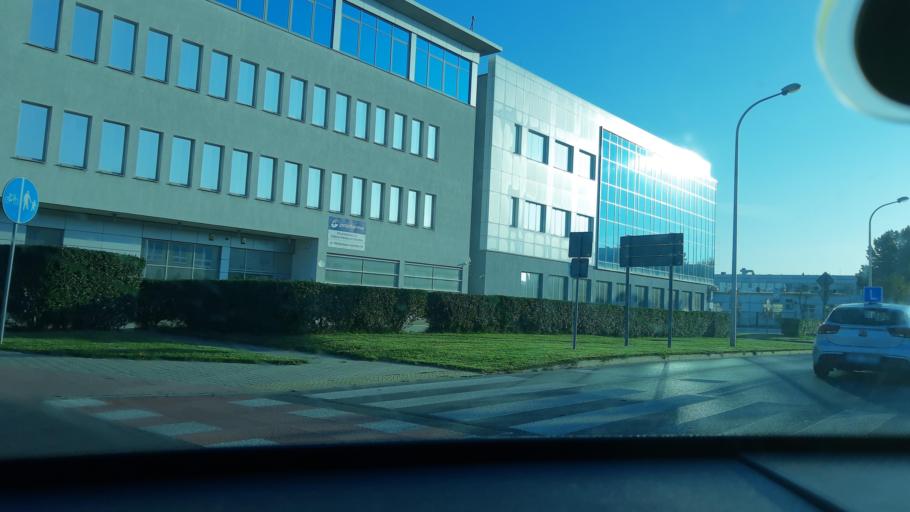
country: PL
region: Lodz Voivodeship
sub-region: Powiat sieradzki
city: Sieradz
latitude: 51.5939
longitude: 18.7153
